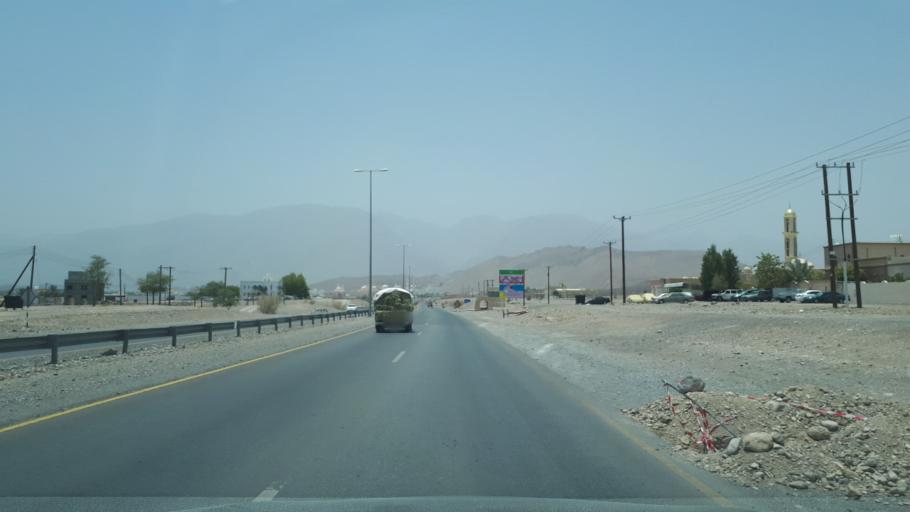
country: OM
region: Al Batinah
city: Rustaq
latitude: 23.4471
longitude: 57.4319
